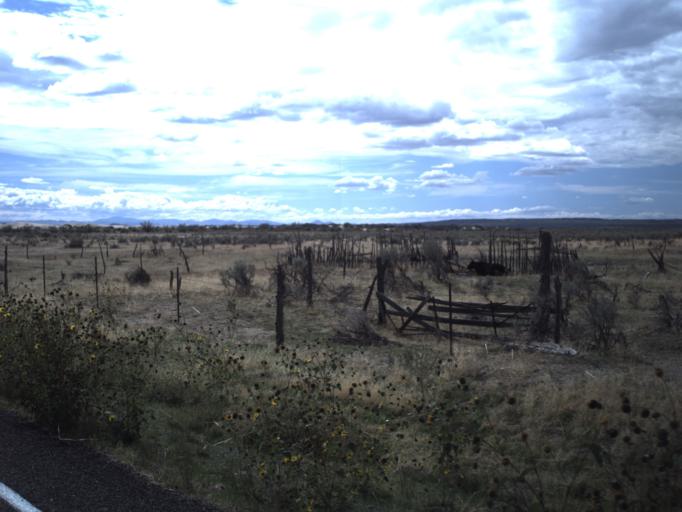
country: US
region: Utah
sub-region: Millard County
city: Fillmore
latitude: 39.1386
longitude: -112.4097
